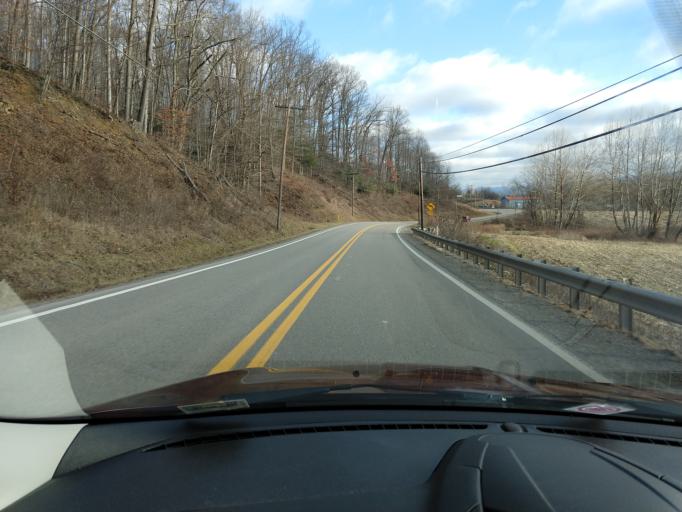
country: US
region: West Virginia
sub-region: Randolph County
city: Elkins
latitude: 38.7482
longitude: -79.9617
